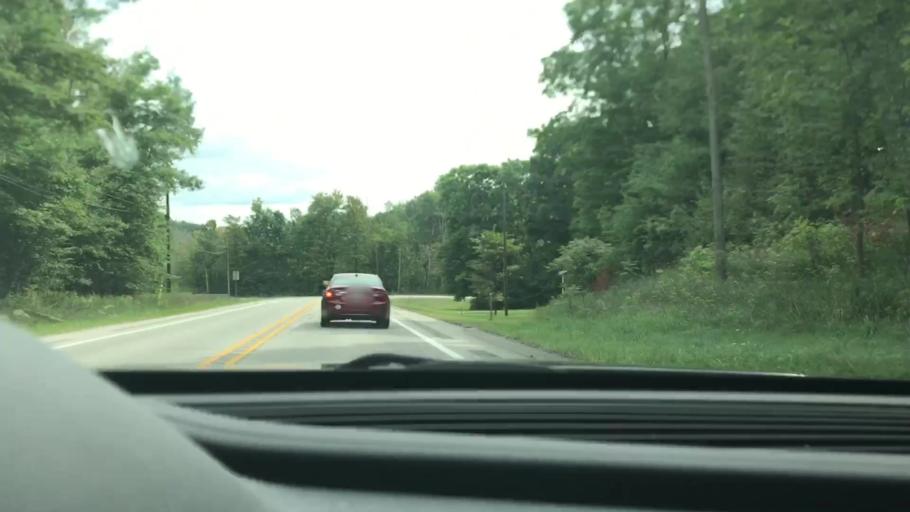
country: US
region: Michigan
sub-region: Antrim County
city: Bellaire
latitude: 45.0802
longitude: -85.2835
